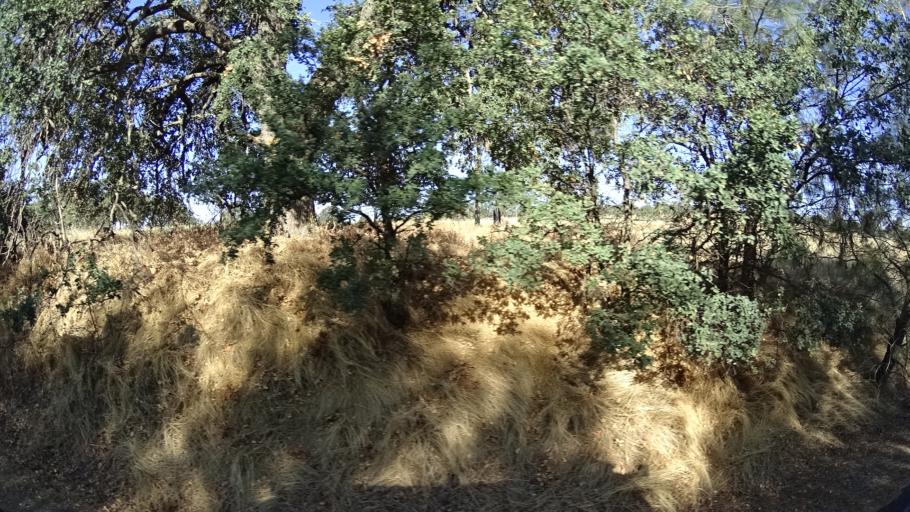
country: US
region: California
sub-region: Calaveras County
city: Valley Springs
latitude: 38.1802
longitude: -120.7942
